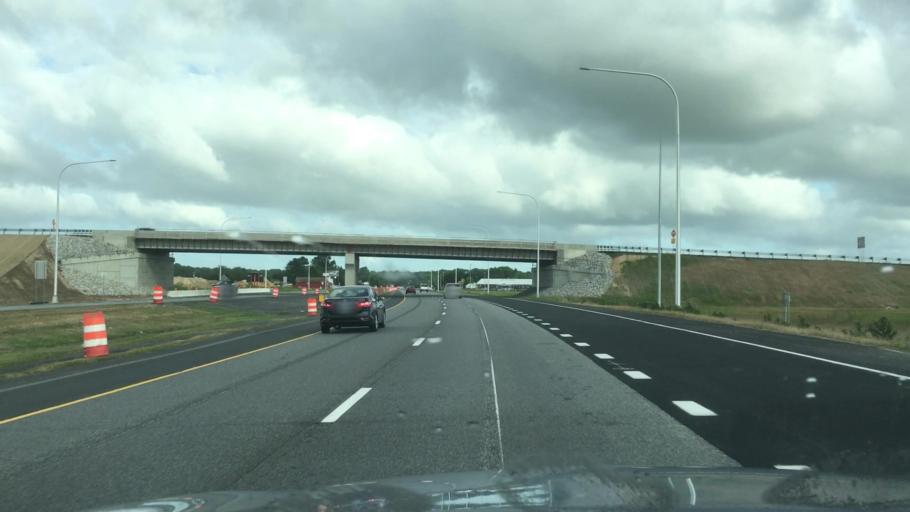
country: US
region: Delaware
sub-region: Kent County
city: Riverview
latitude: 38.9916
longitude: -75.4502
